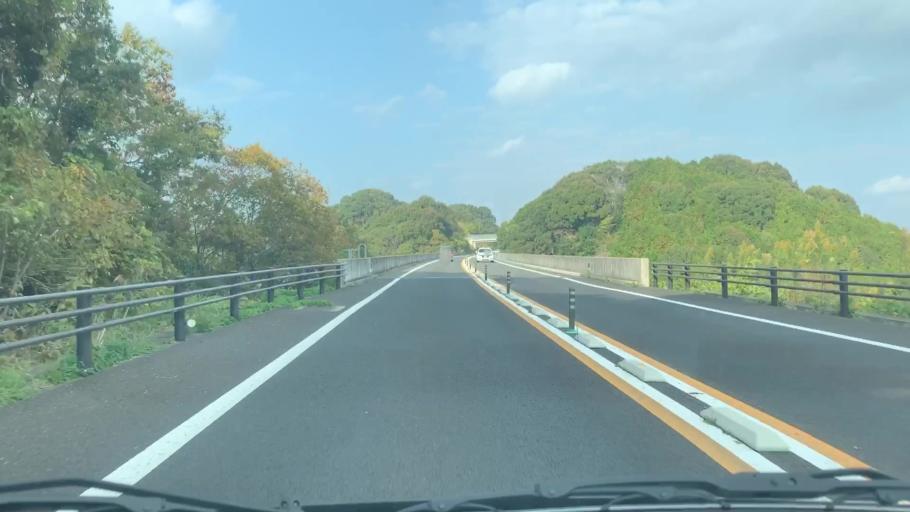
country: JP
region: Nagasaki
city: Sasebo
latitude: 33.0042
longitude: 129.7271
